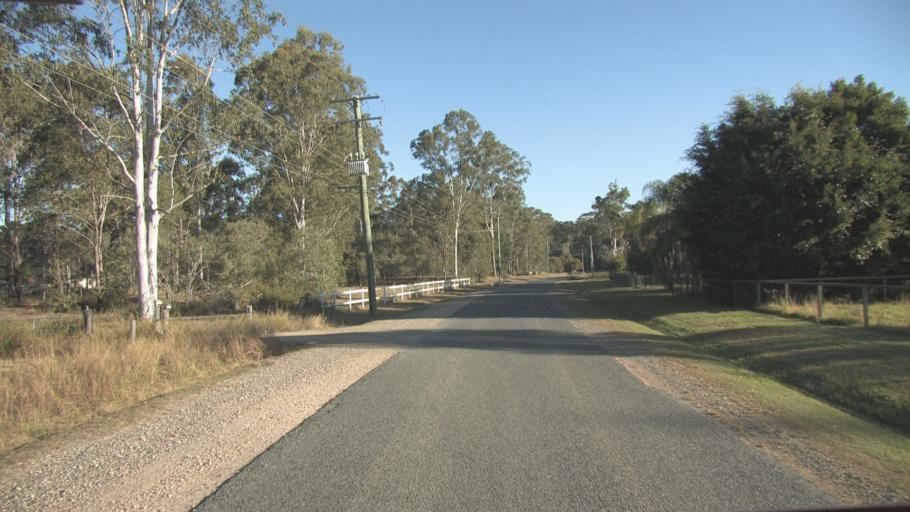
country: AU
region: Queensland
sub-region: Logan
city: Chambers Flat
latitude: -27.7772
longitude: 153.1283
